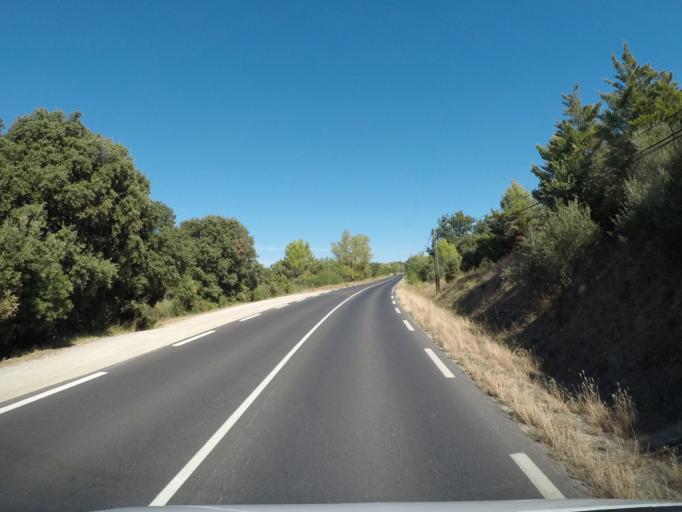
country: FR
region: Languedoc-Roussillon
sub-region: Departement de l'Herault
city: Aniane
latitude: 43.6987
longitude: 3.5913
